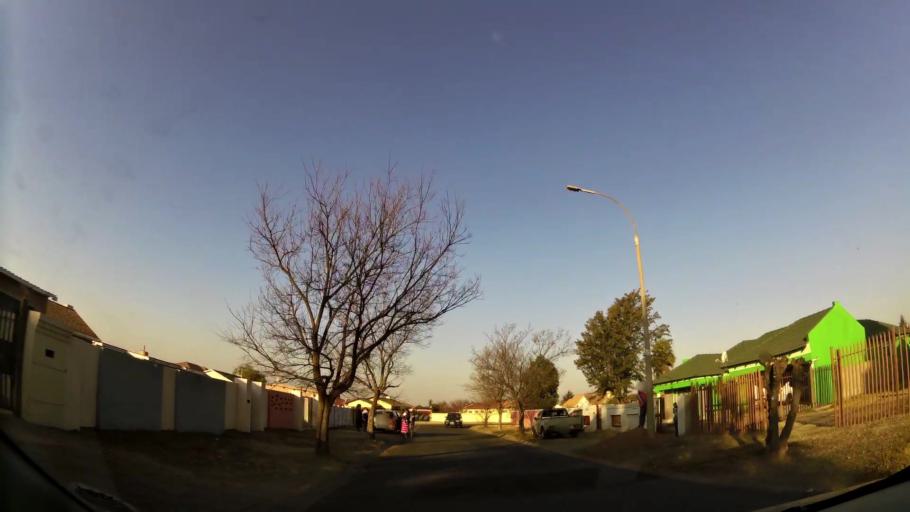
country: ZA
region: Gauteng
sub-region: West Rand District Municipality
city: Randfontein
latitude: -26.2048
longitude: 27.6505
